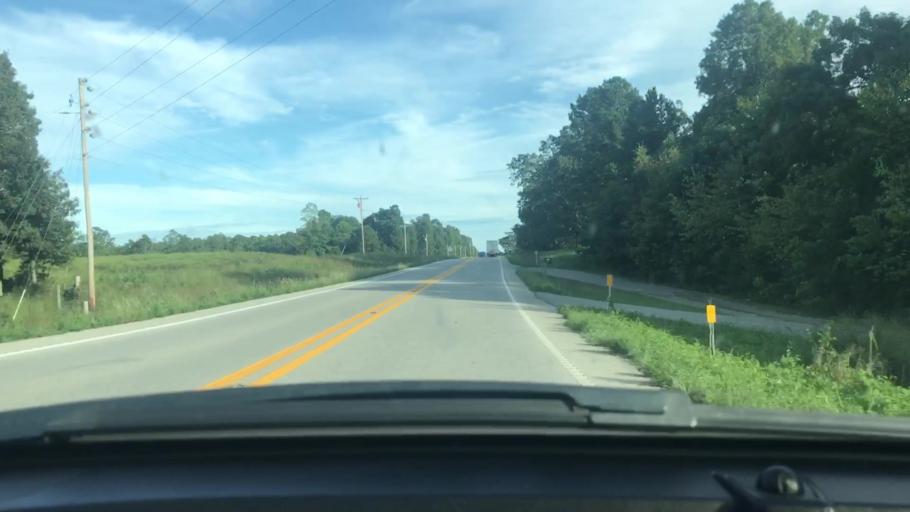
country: US
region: Arkansas
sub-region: Sharp County
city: Cherokee Village
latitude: 36.2749
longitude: -91.3096
